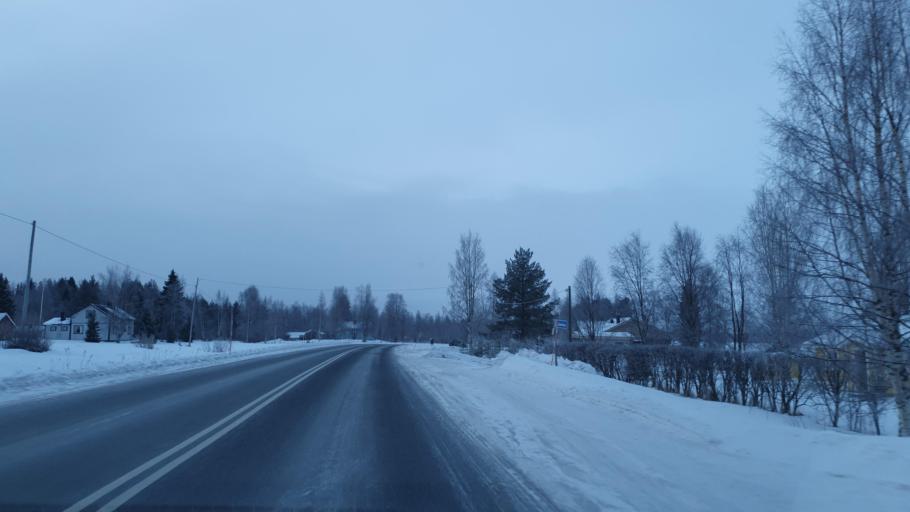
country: FI
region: Lapland
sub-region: Torniolaakso
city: Pello
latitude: 66.6135
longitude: 23.8899
